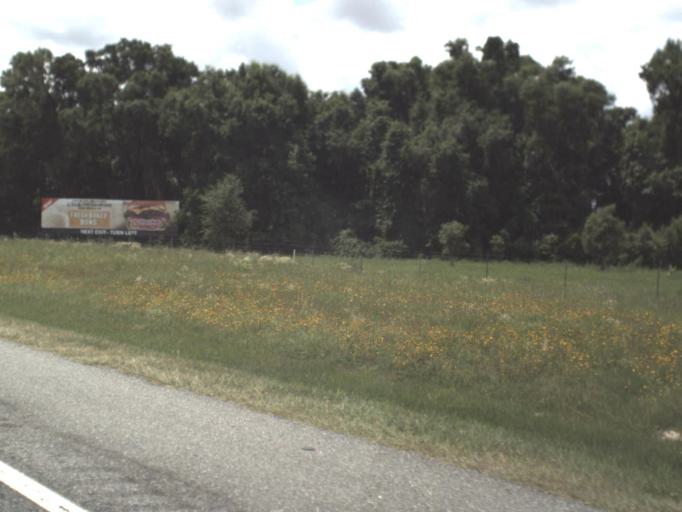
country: US
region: Florida
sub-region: Suwannee County
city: Wellborn
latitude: 30.2378
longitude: -82.7366
